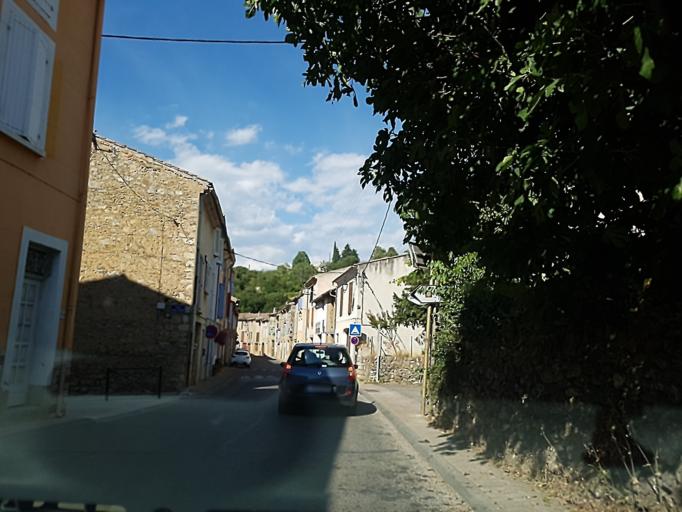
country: FR
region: Provence-Alpes-Cote d'Azur
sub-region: Departement du Var
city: Bras
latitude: 43.4695
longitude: 5.9510
